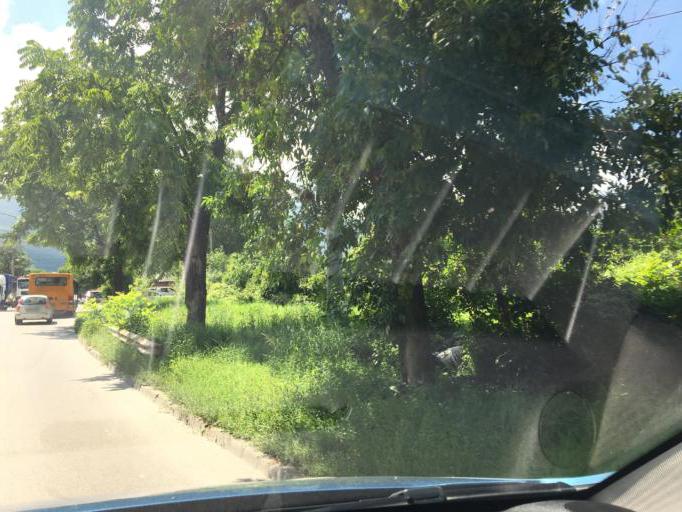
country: BG
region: Sofia-Capital
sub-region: Stolichna Obshtina
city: Sofia
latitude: 42.6282
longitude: 23.3329
